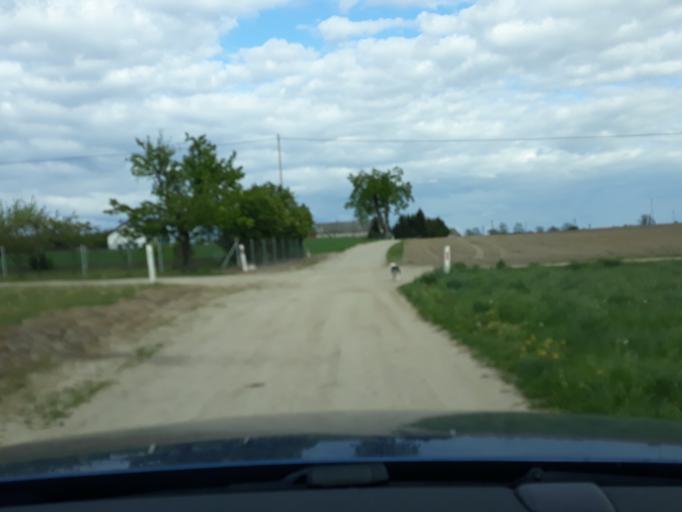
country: PL
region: Pomeranian Voivodeship
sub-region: Powiat czluchowski
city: Czluchow
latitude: 53.7541
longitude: 17.3675
